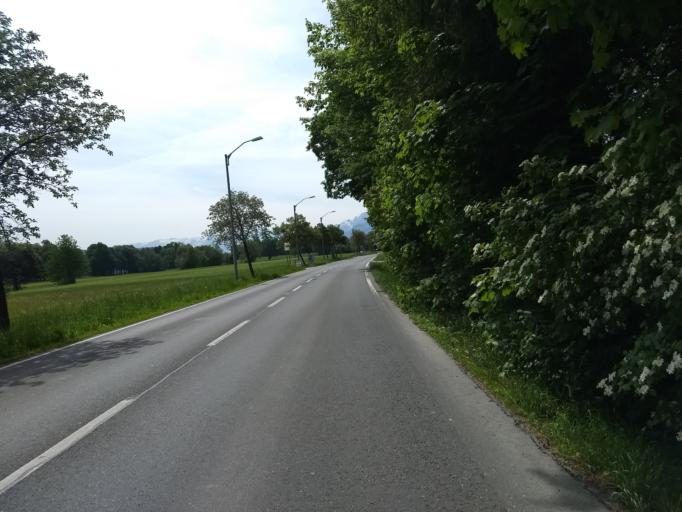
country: AT
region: Salzburg
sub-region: Salzburg Stadt
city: Salzburg
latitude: 47.7782
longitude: 13.0572
